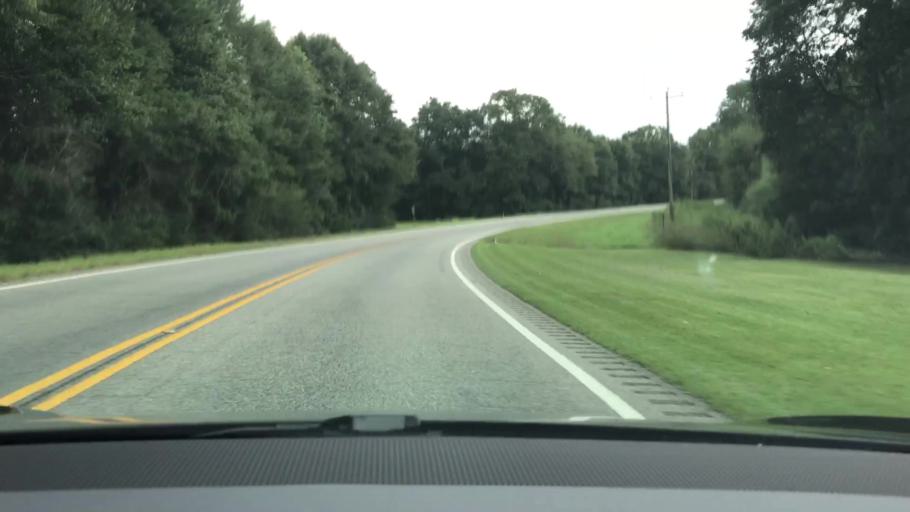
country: US
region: Alabama
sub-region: Coffee County
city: Elba
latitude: 31.5791
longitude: -85.9976
